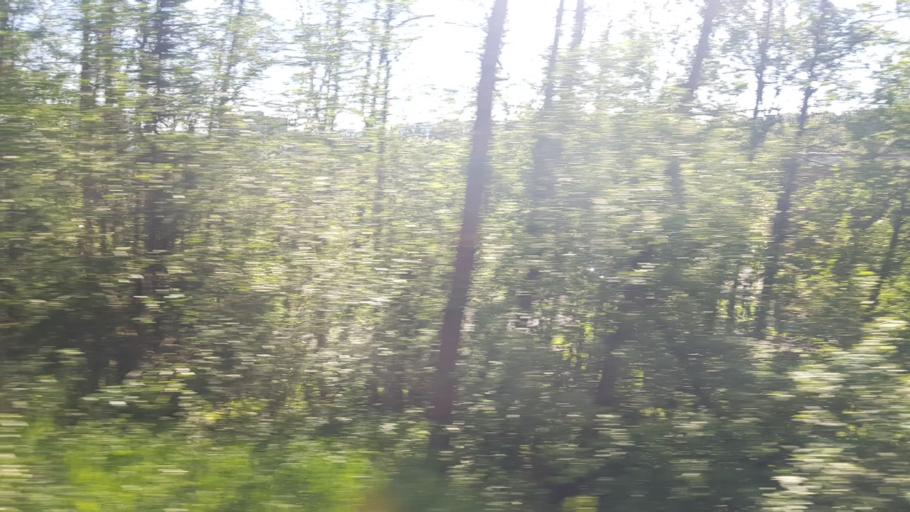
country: NO
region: Sor-Trondelag
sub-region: Trondheim
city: Trondheim
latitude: 63.3785
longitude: 10.3668
